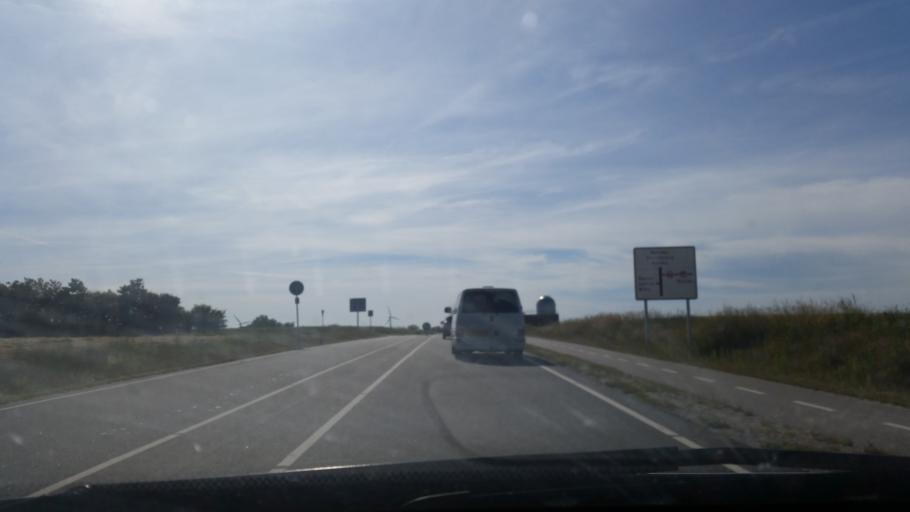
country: DK
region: Central Jutland
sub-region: Samso Kommune
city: Tranebjerg
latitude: 55.8078
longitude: 10.6407
